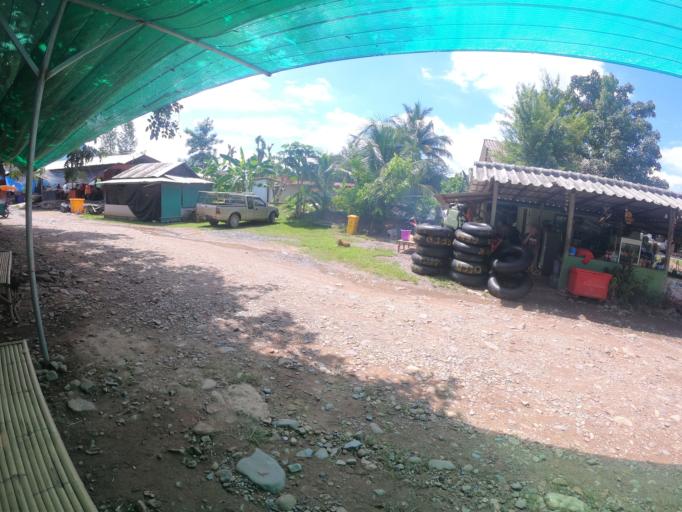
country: TH
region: Nakhon Nayok
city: Nakhon Nayok
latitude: 14.3080
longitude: 101.3116
